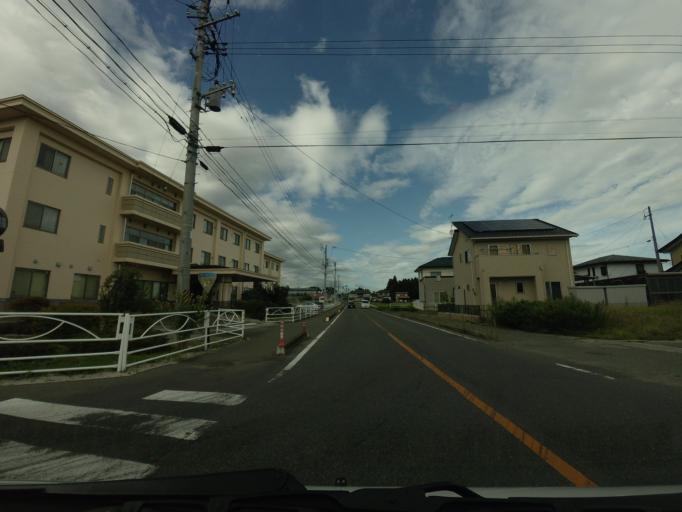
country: JP
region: Fukushima
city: Motomiya
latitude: 37.5323
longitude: 140.3705
